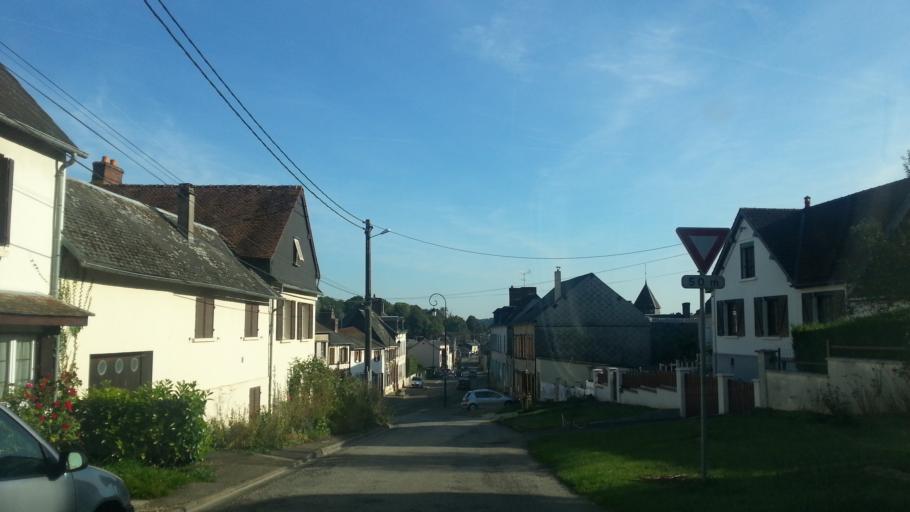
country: FR
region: Picardie
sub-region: Departement de l'Oise
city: Saint-Omer-en-Chaussee
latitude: 49.5777
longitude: 1.9535
